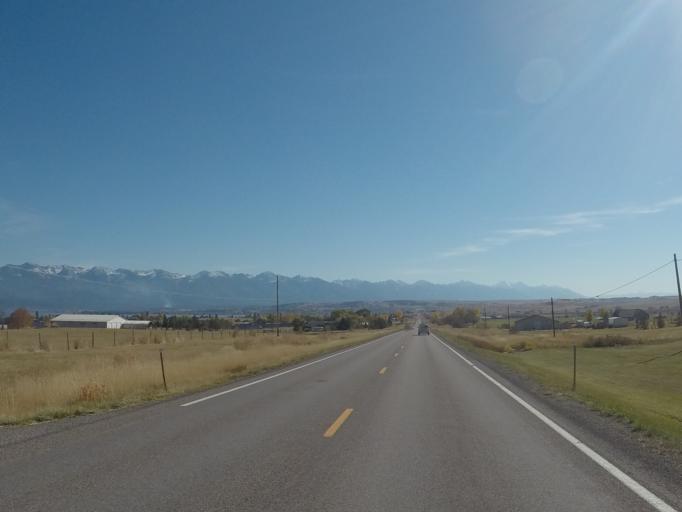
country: US
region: Montana
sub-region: Lake County
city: Polson
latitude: 47.7291
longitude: -114.2129
